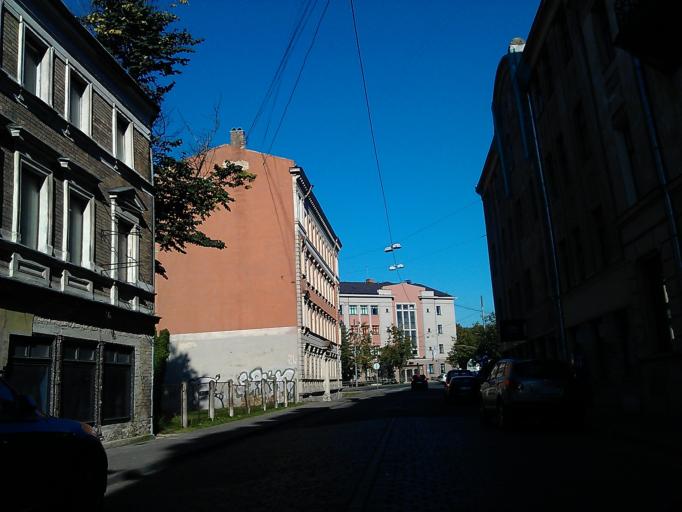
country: LV
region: Riga
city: Riga
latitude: 56.9613
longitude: 24.1069
